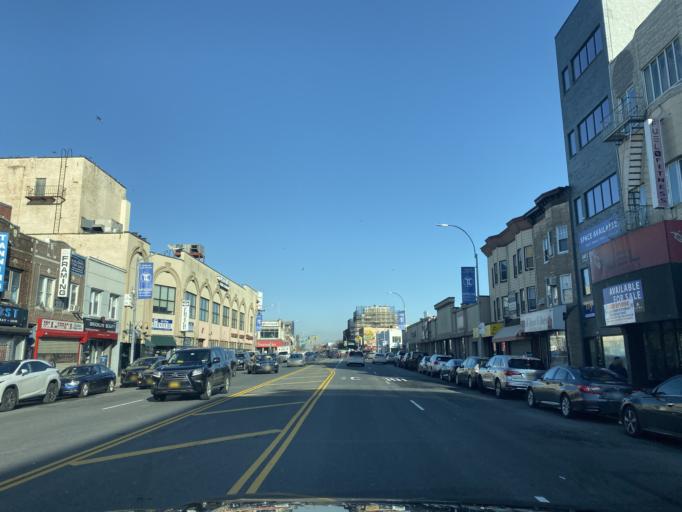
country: US
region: New York
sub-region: Kings County
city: Bensonhurst
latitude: 40.6061
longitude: -73.9617
